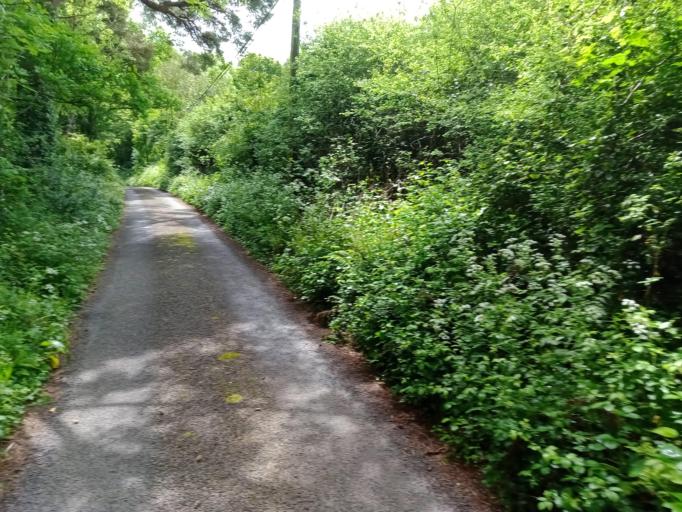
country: IE
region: Leinster
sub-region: Kilkenny
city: Thomastown
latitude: 52.5088
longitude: -7.1308
